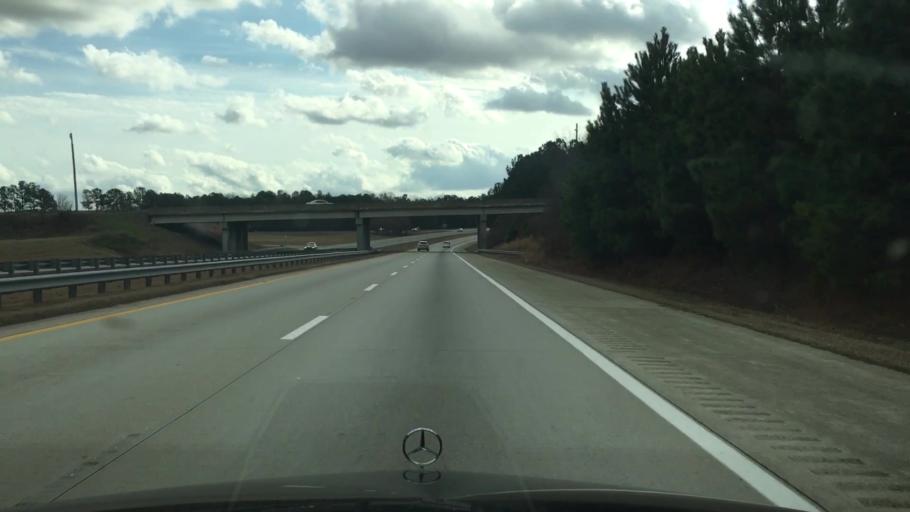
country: US
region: North Carolina
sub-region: Wake County
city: Garner
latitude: 35.6081
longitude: -78.5648
